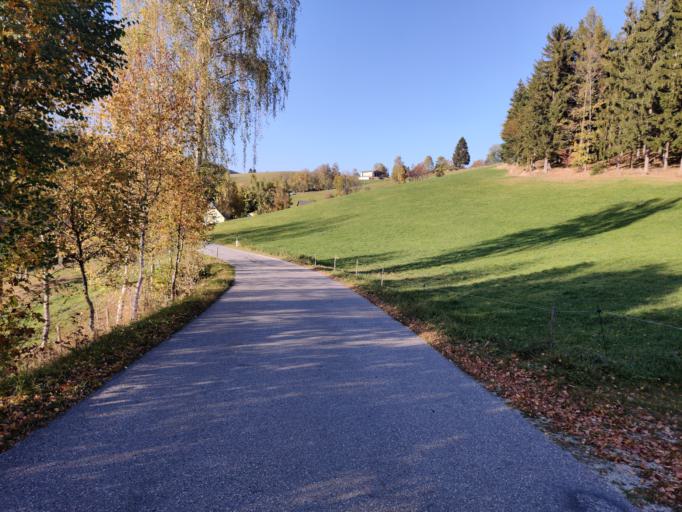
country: AT
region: Styria
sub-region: Politischer Bezirk Hartberg-Fuerstenfeld
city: Sankt Jakob im Walde
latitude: 47.4714
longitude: 15.7973
